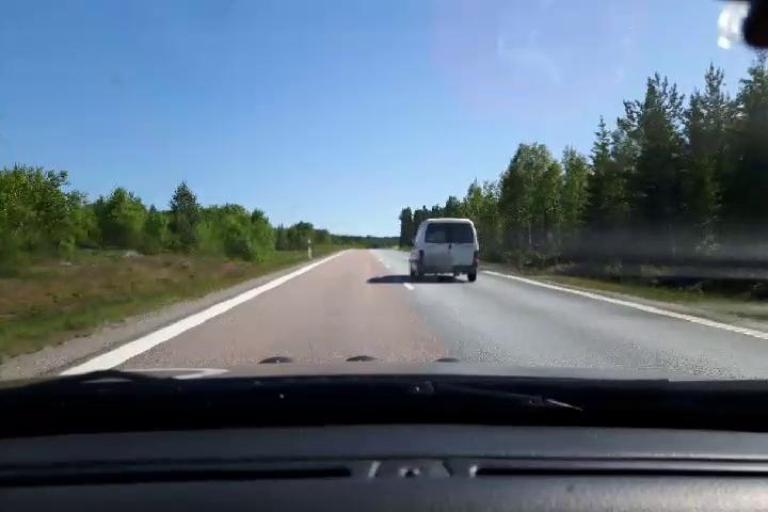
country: SE
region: Gaevleborg
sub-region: Soderhamns Kommun
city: Soderhamn
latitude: 61.4778
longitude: 16.9878
